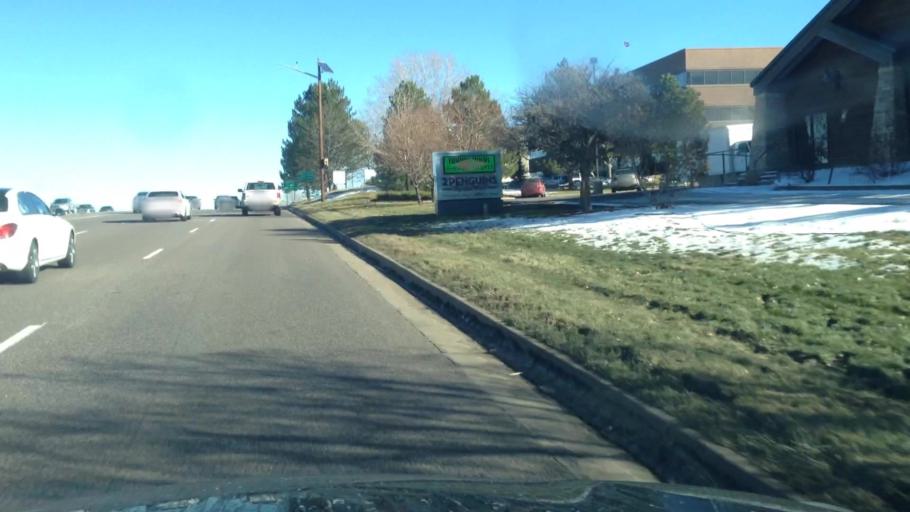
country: US
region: Colorado
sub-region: Arapahoe County
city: Dove Valley
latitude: 39.5949
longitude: -104.8367
